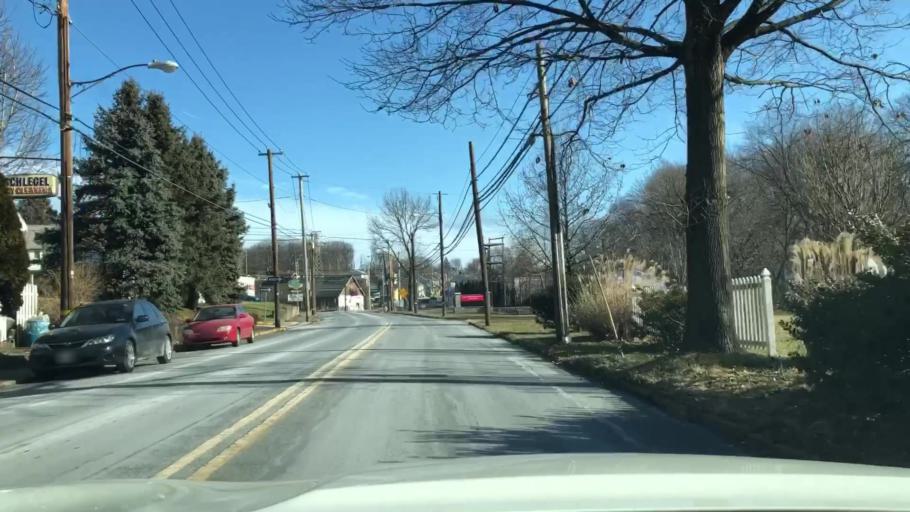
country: US
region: Pennsylvania
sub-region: Lehigh County
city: Catasauqua
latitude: 40.6493
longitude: -75.4676
